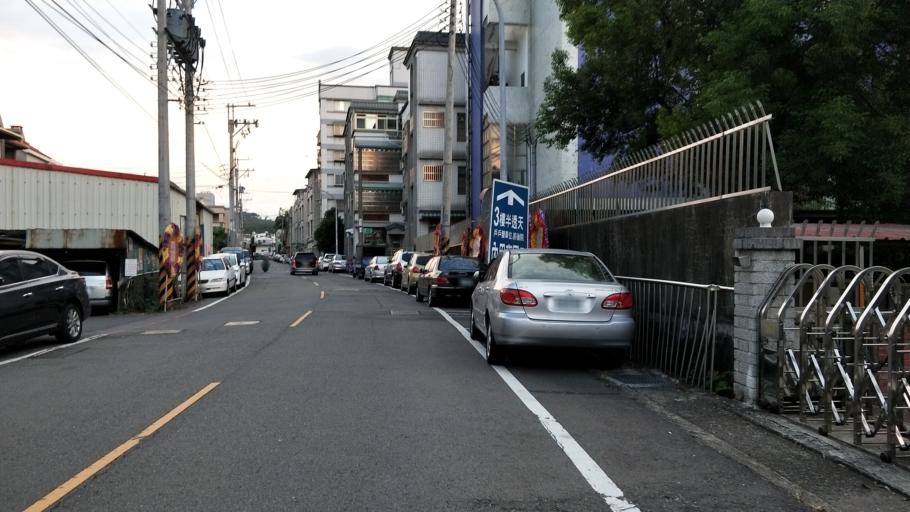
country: TW
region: Taiwan
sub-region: Hsinchu
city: Zhubei
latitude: 24.8278
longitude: 121.0828
